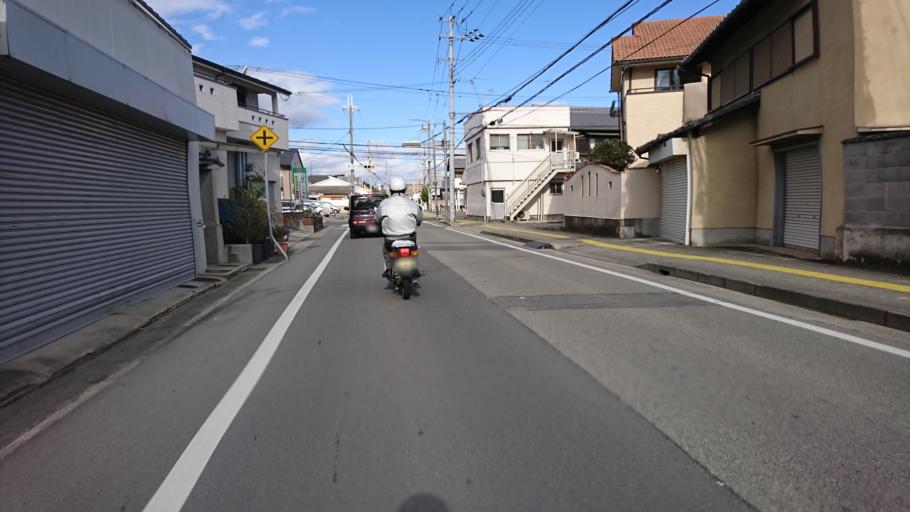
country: JP
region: Hyogo
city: Kakogawacho-honmachi
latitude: 34.7835
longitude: 134.8041
